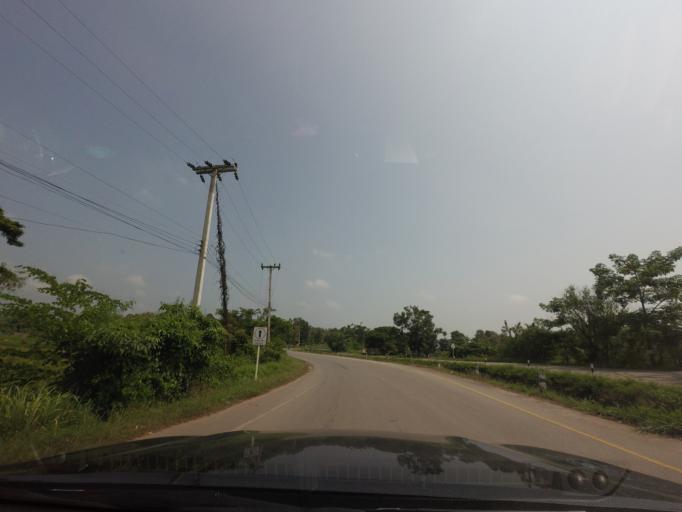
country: TH
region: Nan
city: Nan
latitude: 18.7859
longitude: 100.7450
